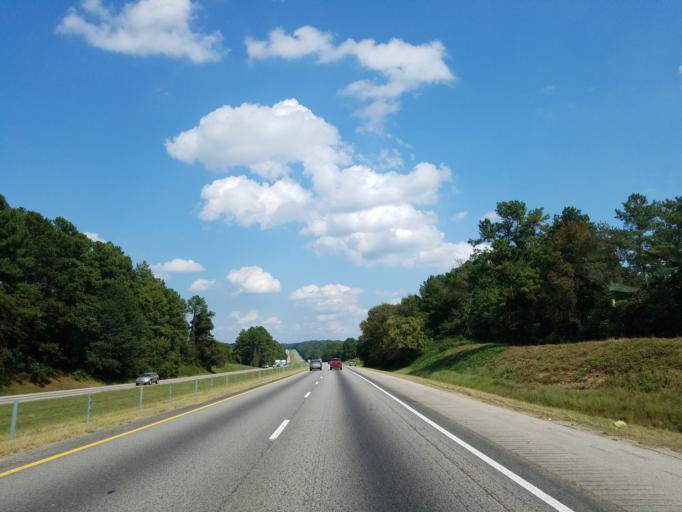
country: US
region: Georgia
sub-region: Jackson County
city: Braselton
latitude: 34.1283
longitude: -83.7103
